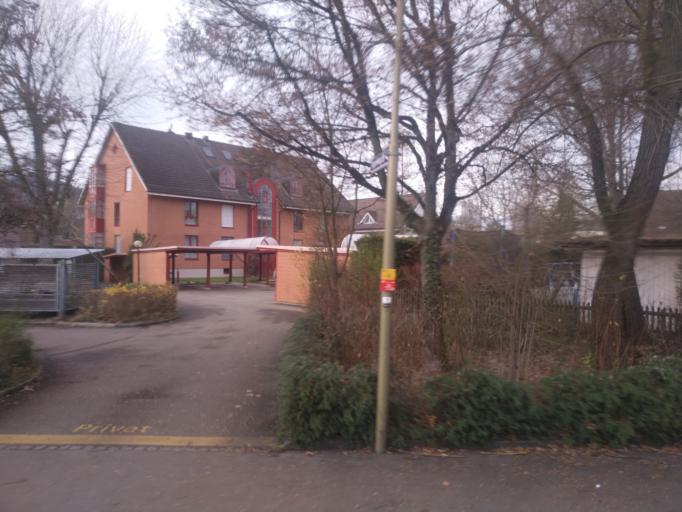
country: CH
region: Zurich
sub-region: Bezirk Winterthur
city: Oberwinterthur (Kreis 2) / Guggenbuehl
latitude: 47.5144
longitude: 8.7627
